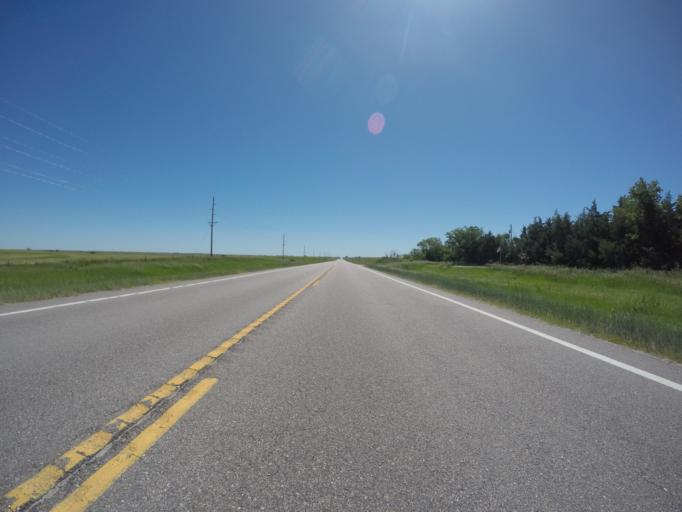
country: US
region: Kansas
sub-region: Norton County
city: Norton
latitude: 39.8283
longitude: -99.6818
